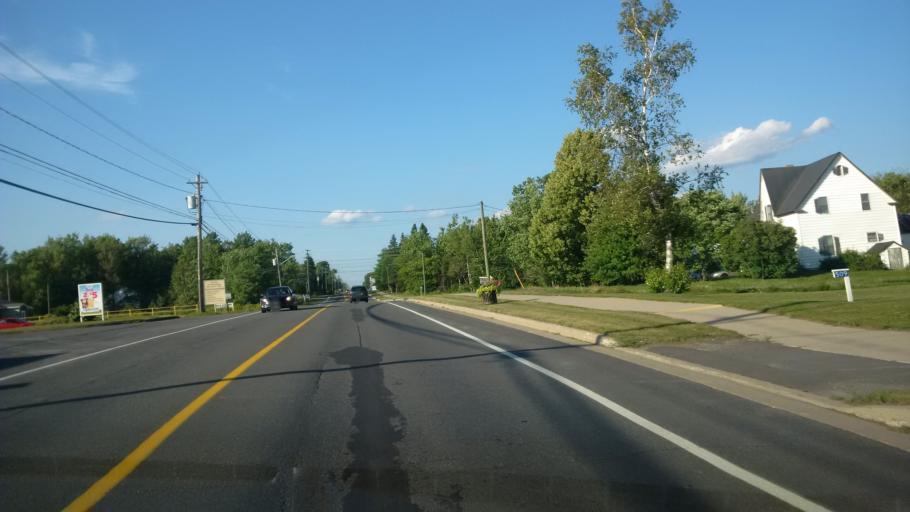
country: CA
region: New Brunswick
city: Fredericton
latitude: 45.8852
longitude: -66.6886
